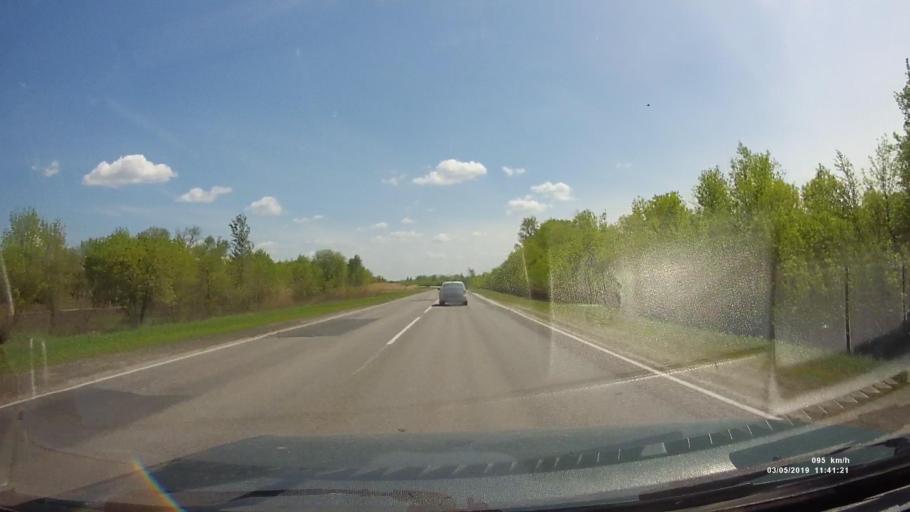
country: RU
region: Rostov
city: Ol'ginskaya
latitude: 47.1374
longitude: 40.0217
